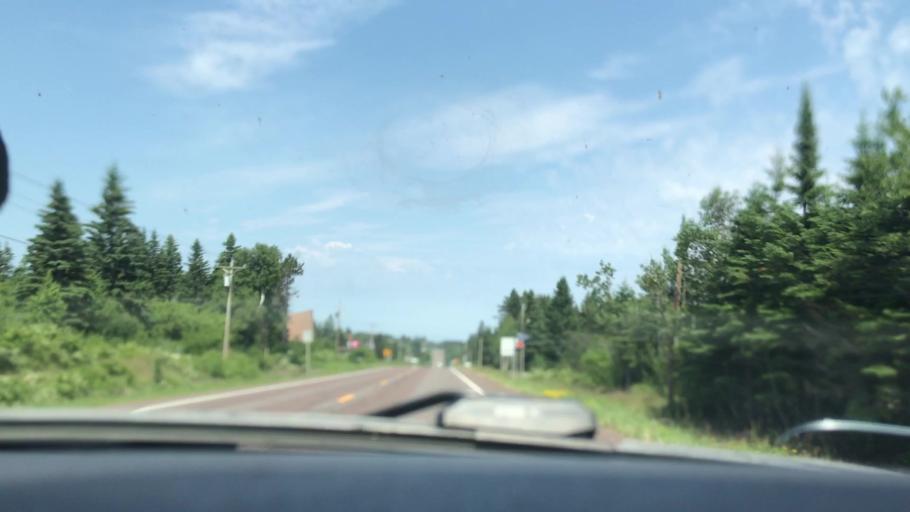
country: US
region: Minnesota
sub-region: Lake County
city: Silver Bay
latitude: 47.5709
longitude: -90.8431
